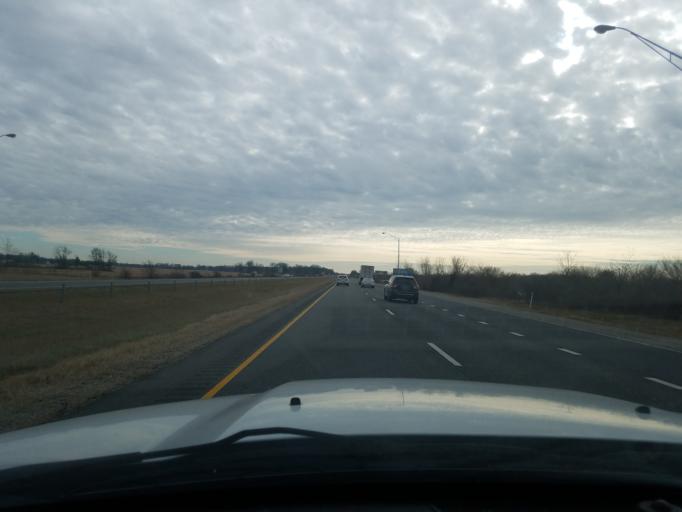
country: US
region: Indiana
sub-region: Delaware County
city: Yorktown
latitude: 40.2724
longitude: -85.5580
